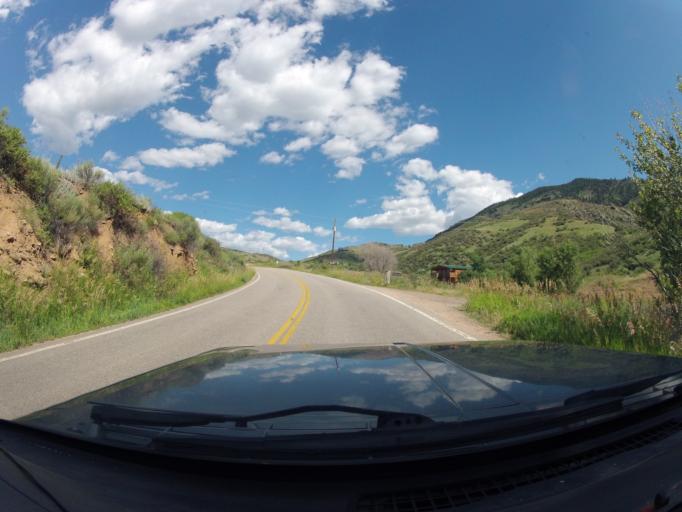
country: US
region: Colorado
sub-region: Larimer County
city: Laporte
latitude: 40.5263
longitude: -105.2618
